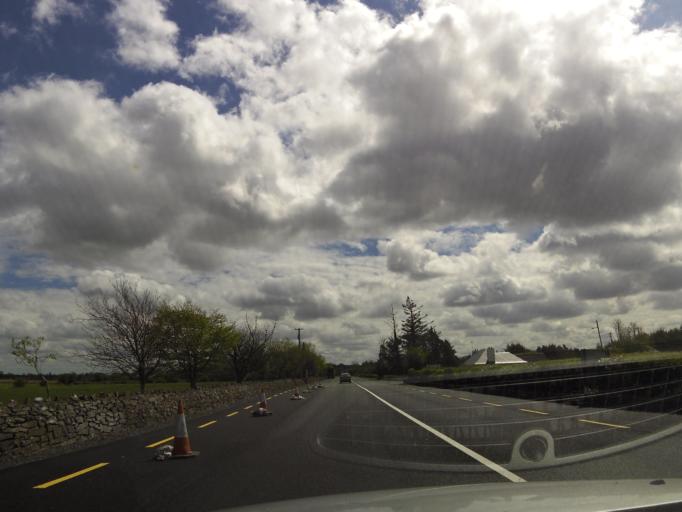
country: IE
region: Connaught
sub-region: County Galway
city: Tuam
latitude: 53.6091
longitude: -8.8942
